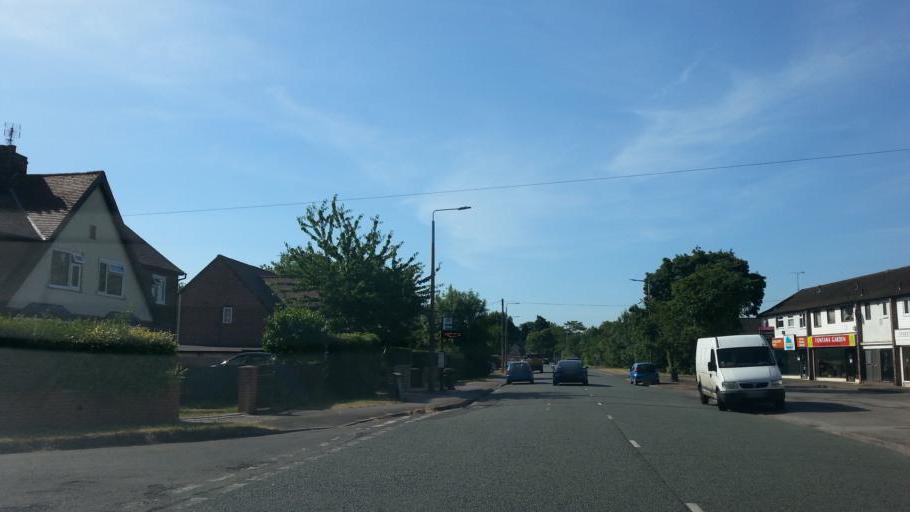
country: GB
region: England
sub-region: Derbyshire
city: Long Eaton
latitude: 52.9113
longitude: -1.2370
